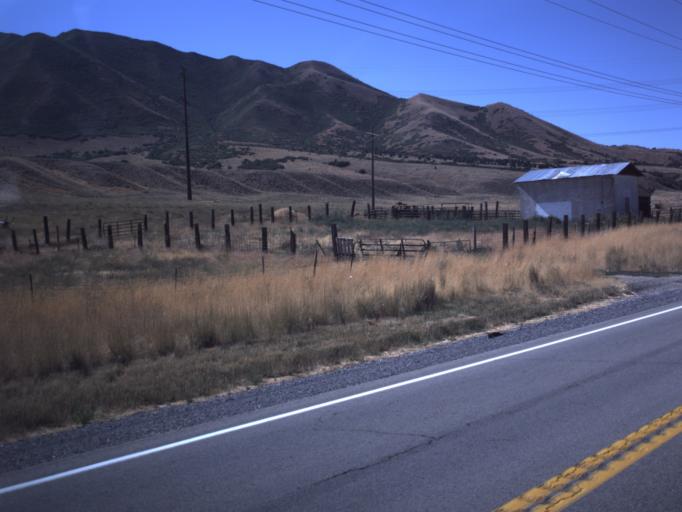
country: US
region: Utah
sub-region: Tooele County
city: Tooele
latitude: 40.4952
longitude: -112.3296
